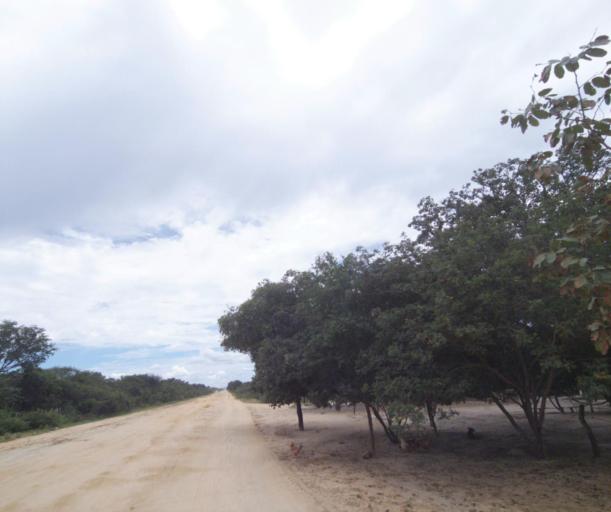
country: BR
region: Bahia
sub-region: Carinhanha
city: Carinhanha
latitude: -14.2737
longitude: -43.8033
